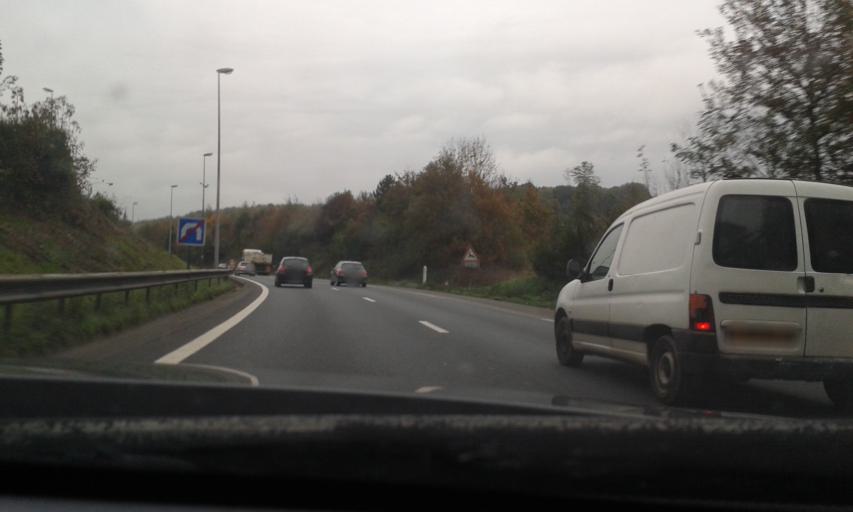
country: FR
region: Haute-Normandie
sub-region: Departement de la Seine-Maritime
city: Bihorel
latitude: 49.4405
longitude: 1.1325
